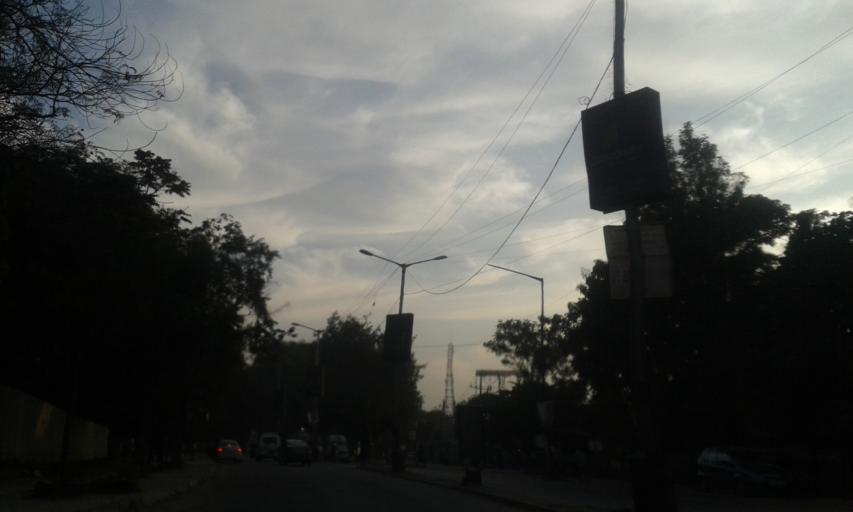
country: IN
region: Karnataka
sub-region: Bangalore Rural
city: Hoskote
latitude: 12.9941
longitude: 77.7577
